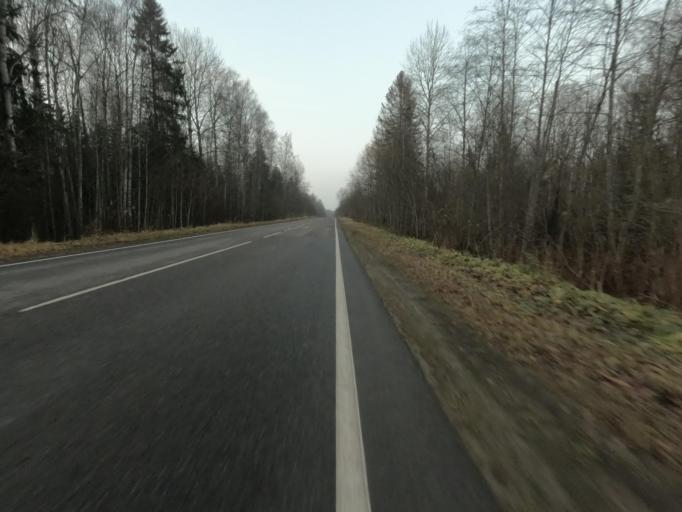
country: RU
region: Leningrad
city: Kirovsk
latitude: 59.8530
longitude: 30.9921
